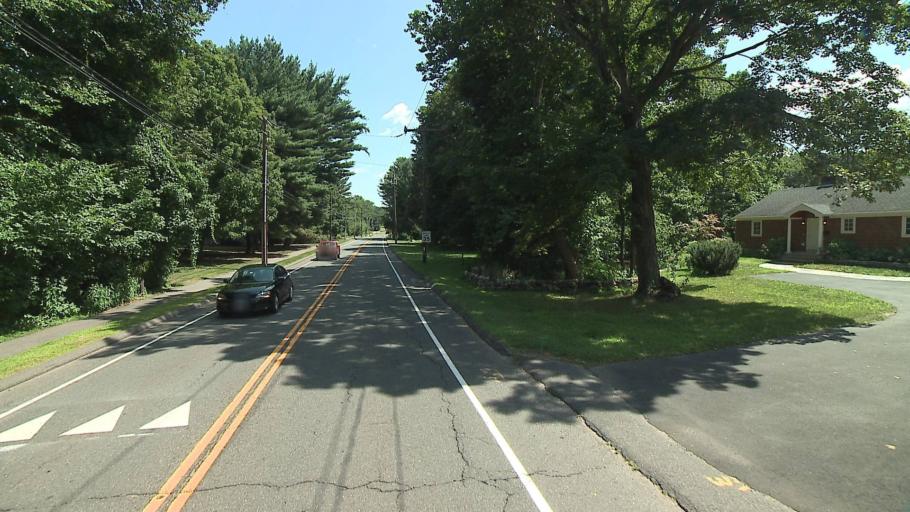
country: US
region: Connecticut
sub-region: Hartford County
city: Farmington
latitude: 41.7526
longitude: -72.8740
